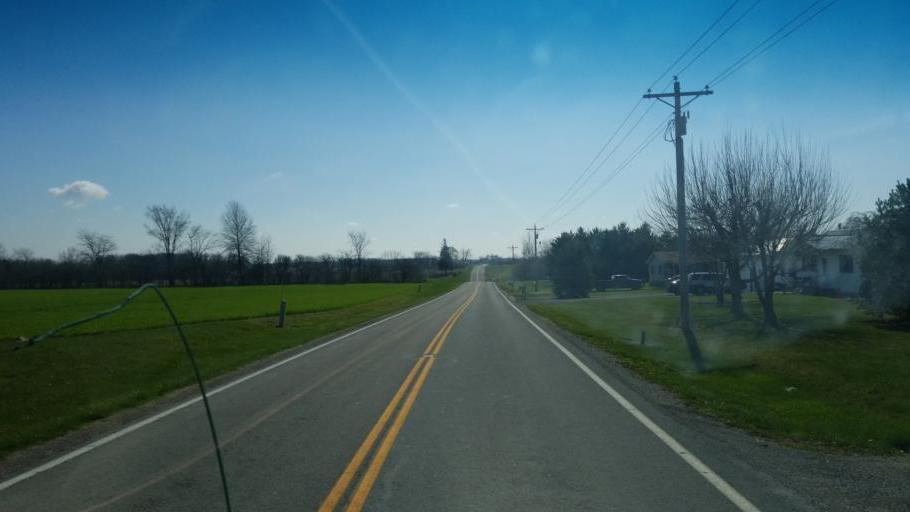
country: US
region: Ohio
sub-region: Wyandot County
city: Upper Sandusky
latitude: 40.7382
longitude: -83.3809
